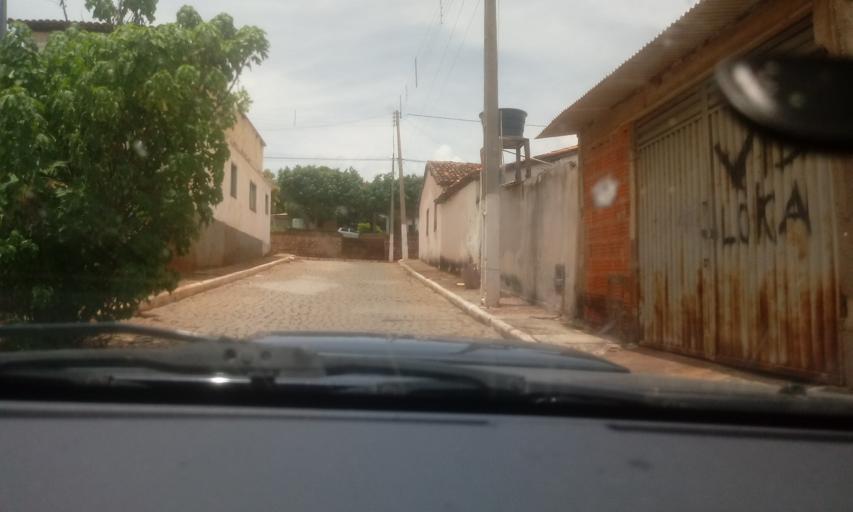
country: BR
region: Bahia
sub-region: Riacho De Santana
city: Riacho de Santana
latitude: -13.6098
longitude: -42.9389
